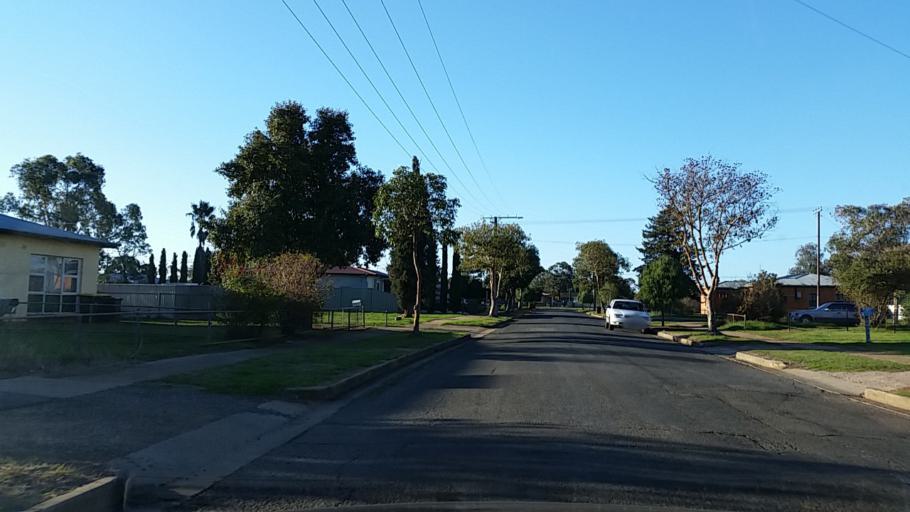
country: AU
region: South Australia
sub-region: Playford
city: Smithfield
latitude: -34.6844
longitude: 138.6665
